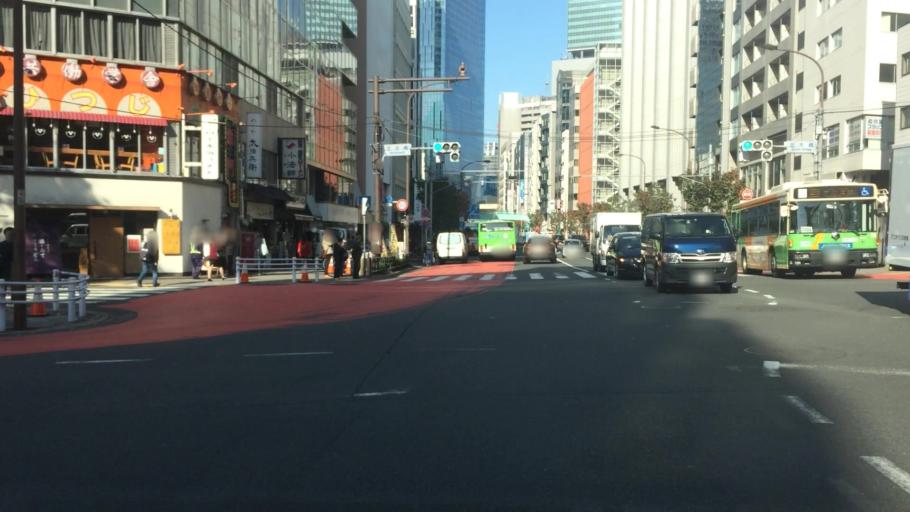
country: JP
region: Tokyo
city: Tokyo
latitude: 35.6551
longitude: 139.7067
